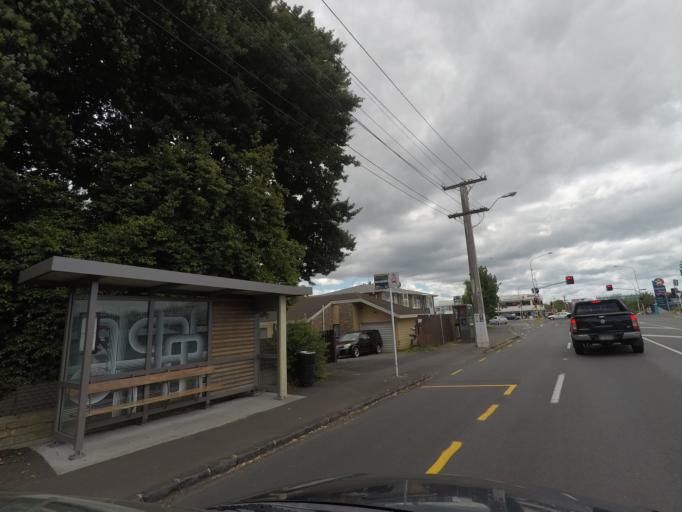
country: NZ
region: Auckland
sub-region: Auckland
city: Auckland
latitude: -36.8859
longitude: 174.7382
